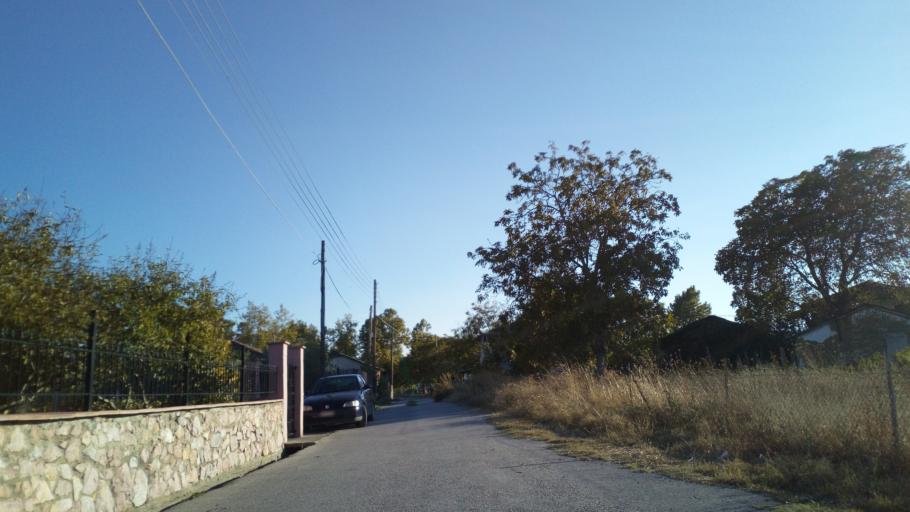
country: GR
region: Central Macedonia
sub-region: Nomos Thessalonikis
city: Gerakarou
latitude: 40.6381
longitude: 23.2450
